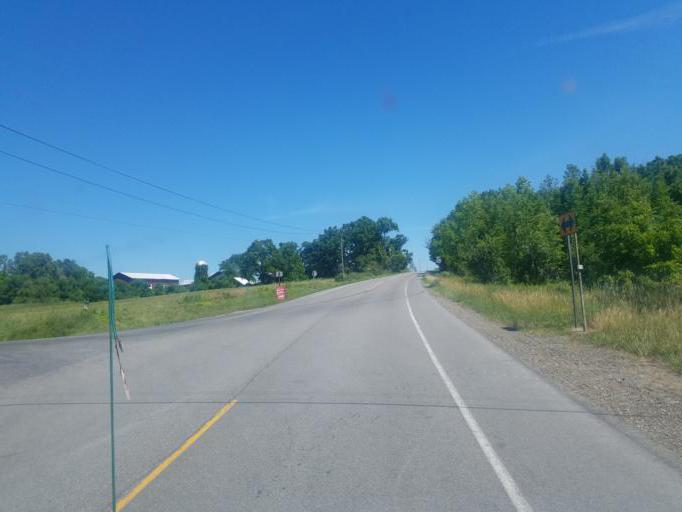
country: US
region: New York
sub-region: Ontario County
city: Canandaigua
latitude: 42.7255
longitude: -77.2794
